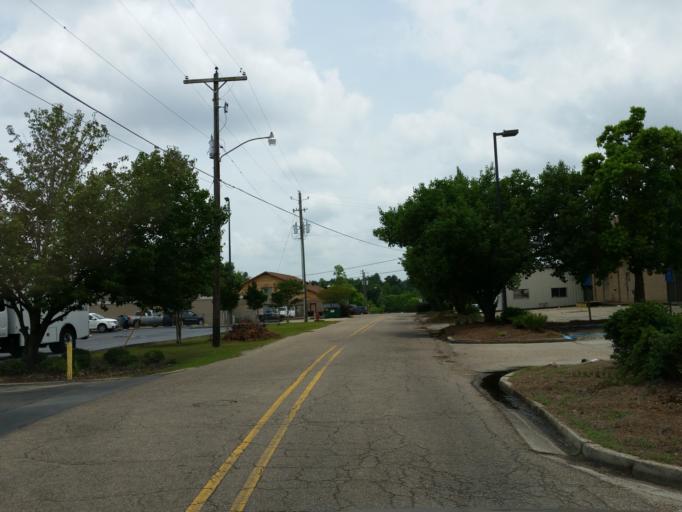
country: US
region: Mississippi
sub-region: Lamar County
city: West Hattiesburg
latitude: 31.3241
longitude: -89.3490
